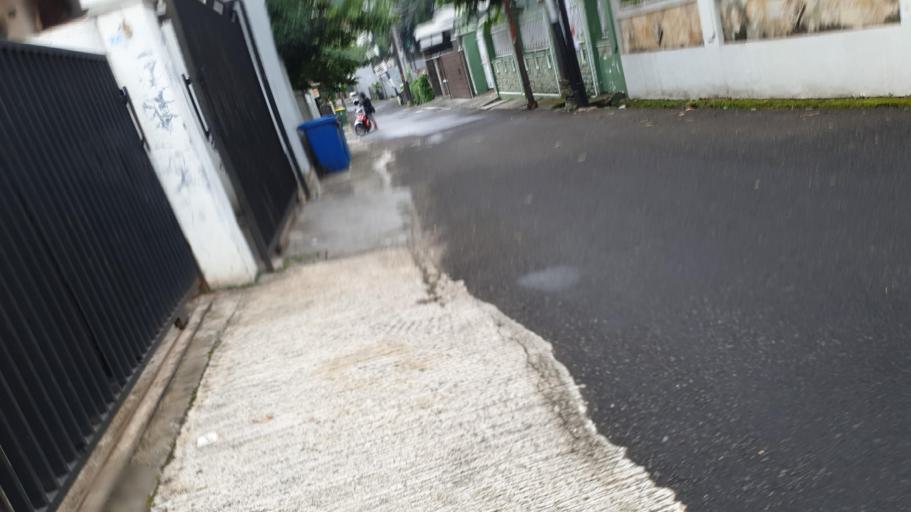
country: ID
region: Banten
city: South Tangerang
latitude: -6.2619
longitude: 106.7864
